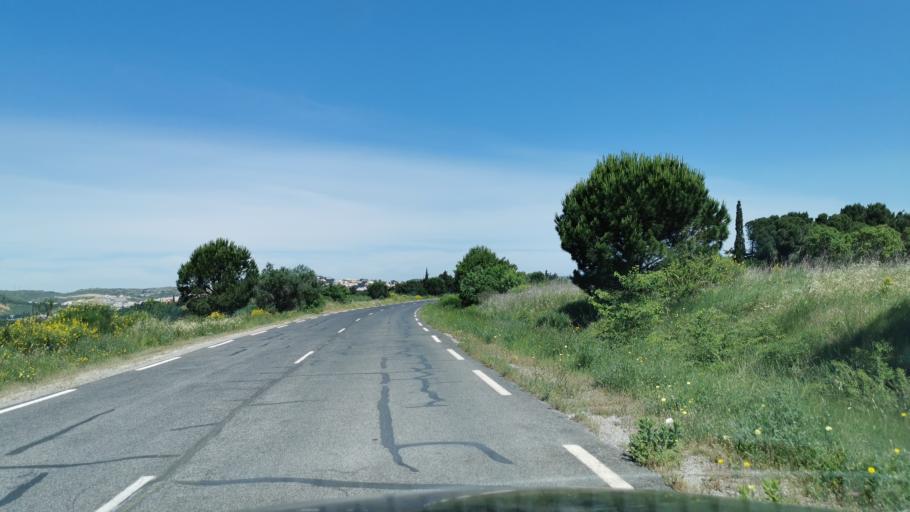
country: FR
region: Languedoc-Roussillon
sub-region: Departement de l'Aude
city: Narbonne
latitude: 43.1504
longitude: 2.9998
